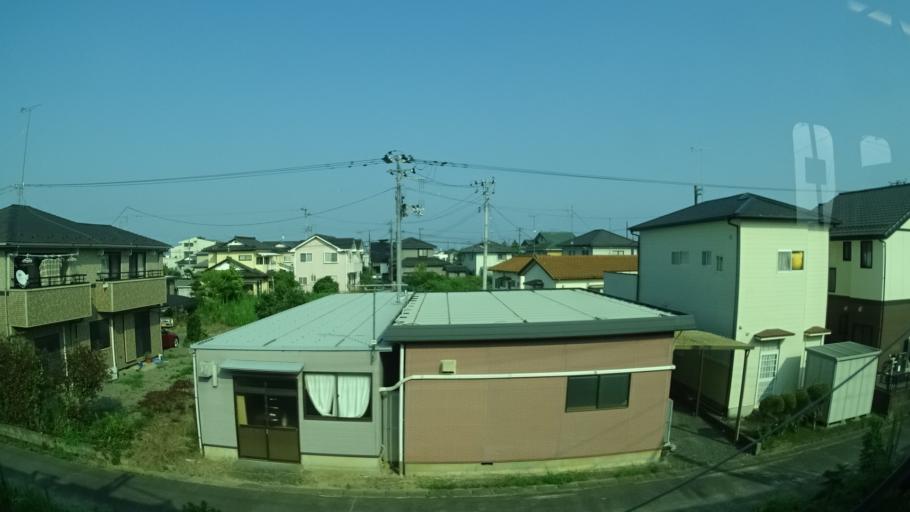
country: JP
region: Ibaraki
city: Kitaibaraki
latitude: 36.9063
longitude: 140.7866
